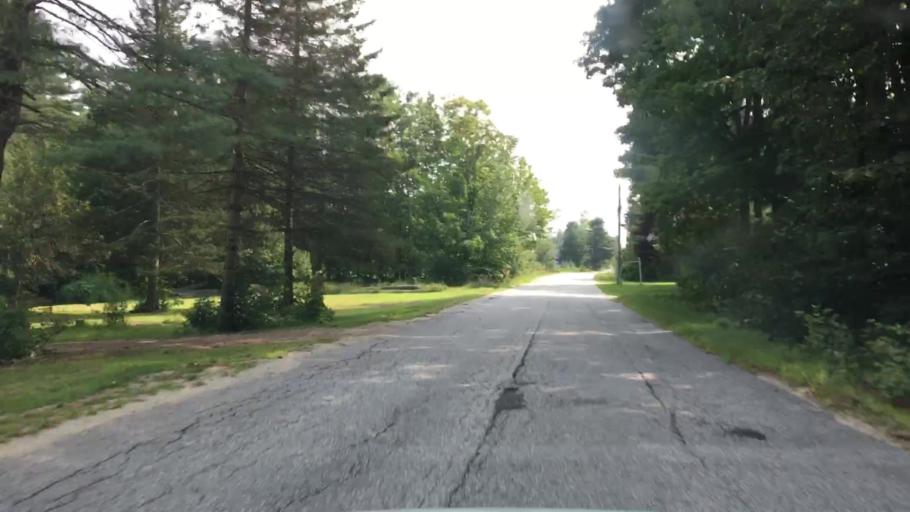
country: US
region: Maine
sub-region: Androscoggin County
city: Livermore
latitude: 44.3284
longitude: -70.2898
